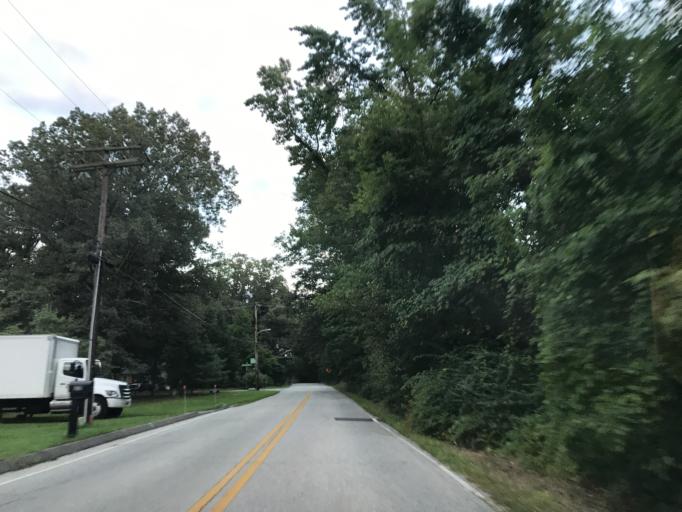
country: US
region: Maryland
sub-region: Anne Arundel County
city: Pasadena
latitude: 39.1003
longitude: -76.5713
